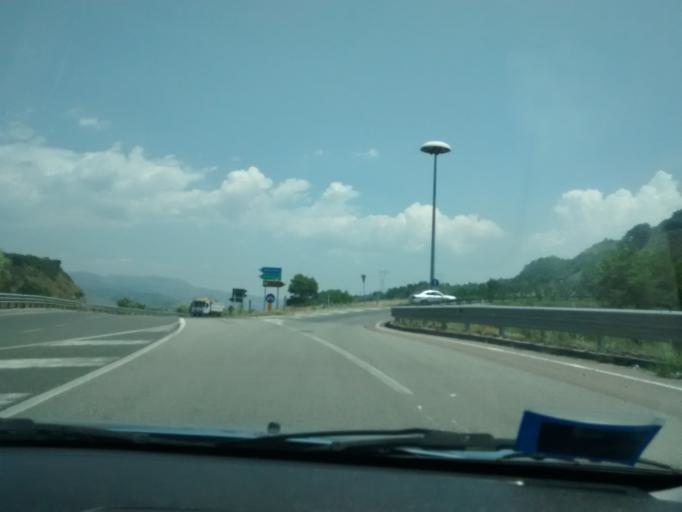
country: IT
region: Calabria
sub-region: Provincia di Catanzaro
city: Maida
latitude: 38.9016
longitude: 16.3878
